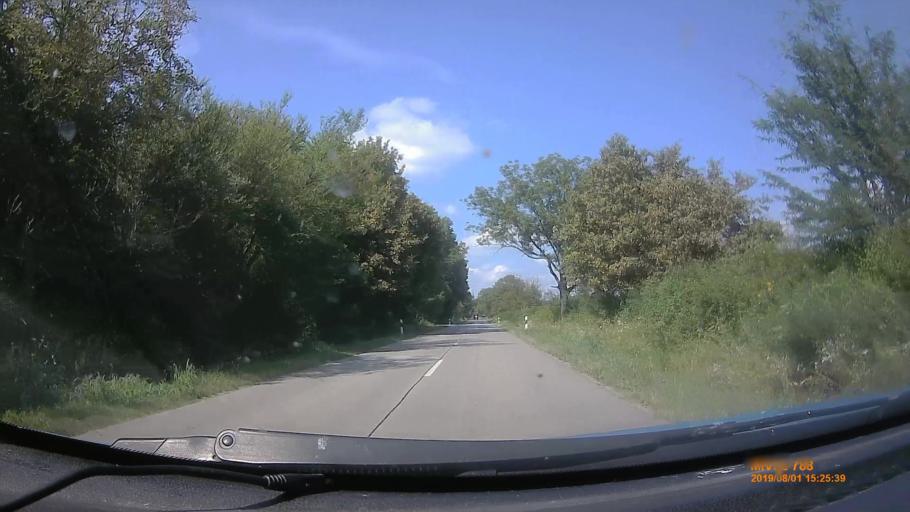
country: HU
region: Baranya
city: Sellye
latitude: 45.8957
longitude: 17.8554
